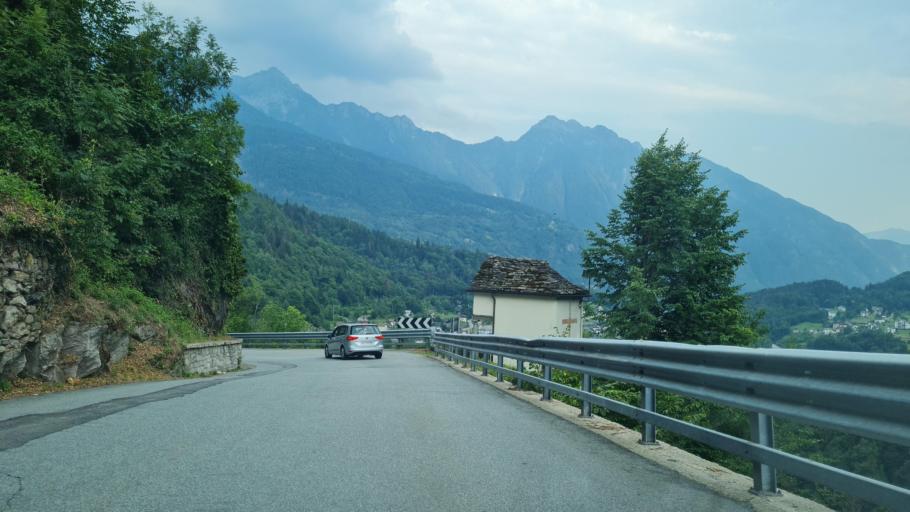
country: IT
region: Piedmont
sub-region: Provincia Verbano-Cusio-Ossola
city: Baceno
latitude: 46.2705
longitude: 8.3079
